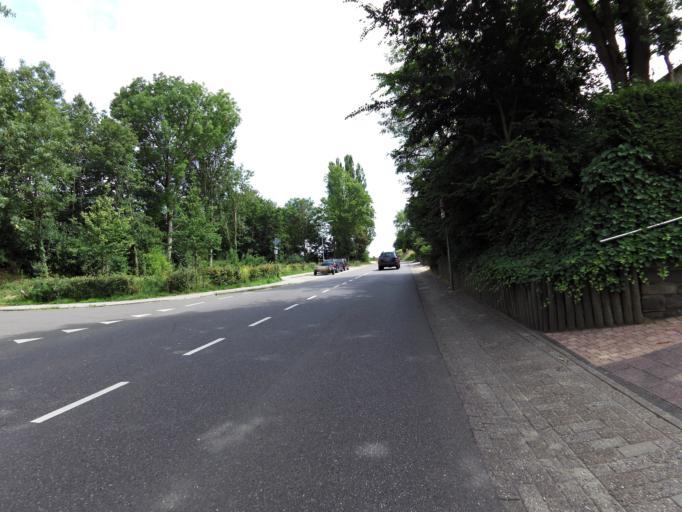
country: NL
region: Limburg
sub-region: Gemeente Voerendaal
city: Ubachsberg
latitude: 50.8077
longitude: 5.9216
